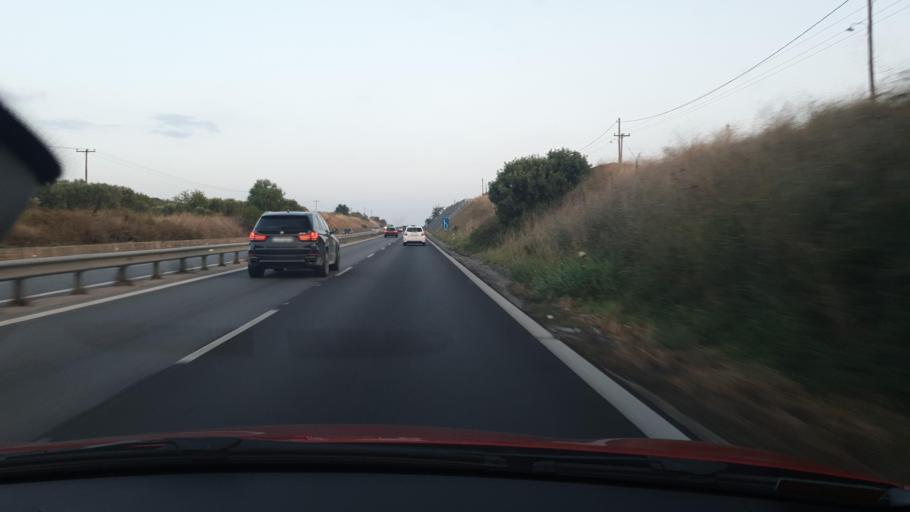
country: GR
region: Central Macedonia
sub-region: Nomos Chalkidikis
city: Nea Moudhania
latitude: 40.2504
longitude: 23.2919
